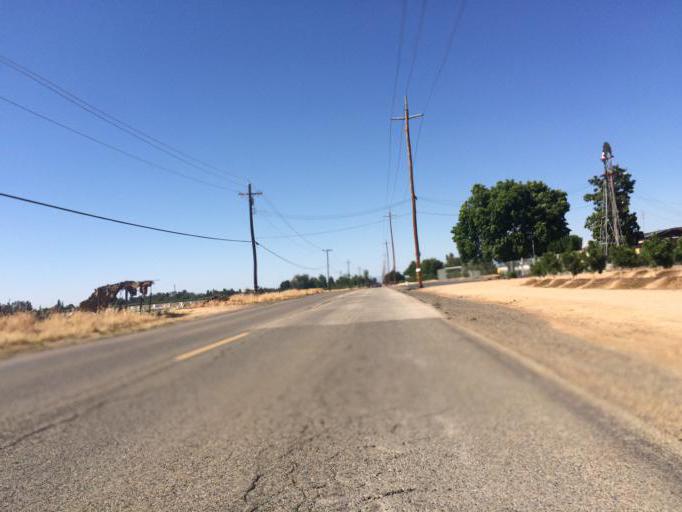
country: US
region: California
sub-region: Fresno County
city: Sanger
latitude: 36.7400
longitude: -119.6101
